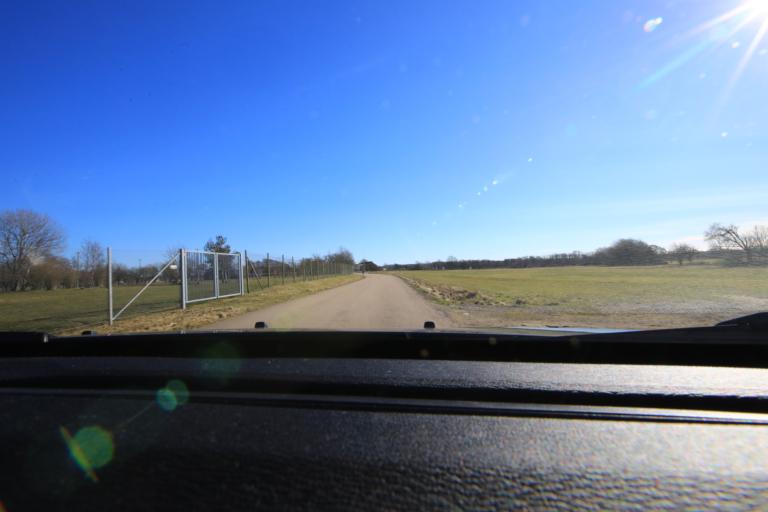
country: SE
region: Halland
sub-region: Varbergs Kommun
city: Tvaaker
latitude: 57.0447
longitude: 12.3771
